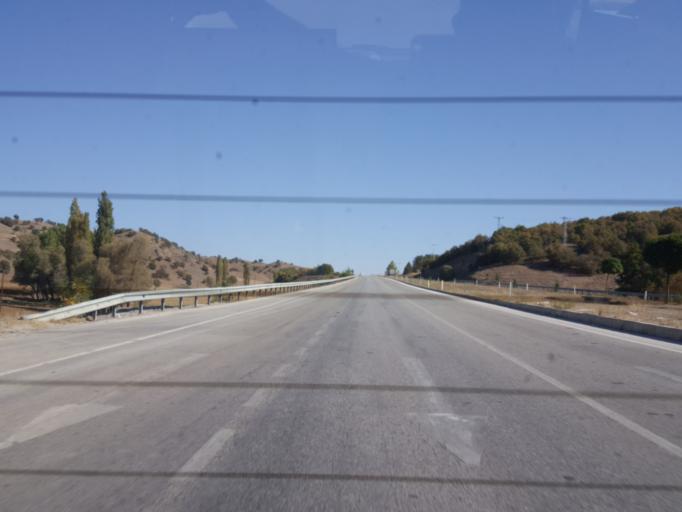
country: TR
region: Corum
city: Alaca
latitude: 40.2756
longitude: 34.6419
